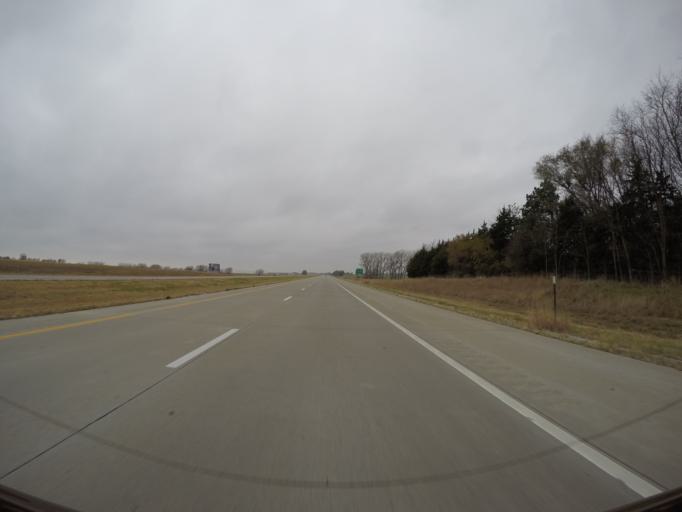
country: US
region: Kansas
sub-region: Dickinson County
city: Abilene
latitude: 38.9376
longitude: -97.2424
